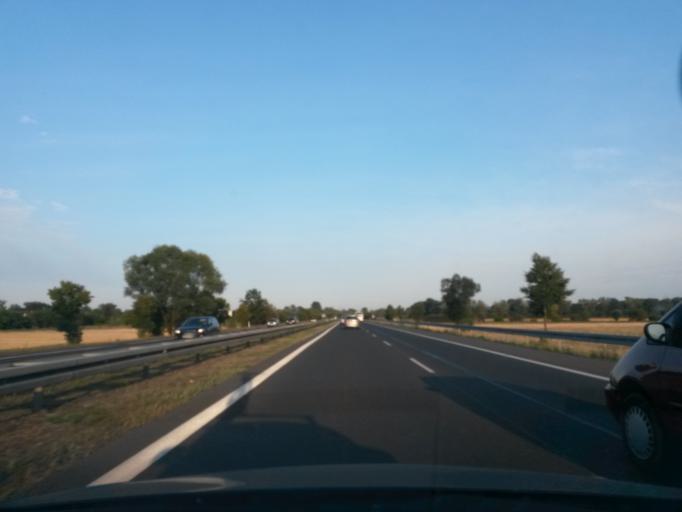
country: PL
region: Masovian Voivodeship
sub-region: Powiat nowodworski
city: Nowy Dwor Mazowiecki
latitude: 52.4166
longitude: 20.6794
